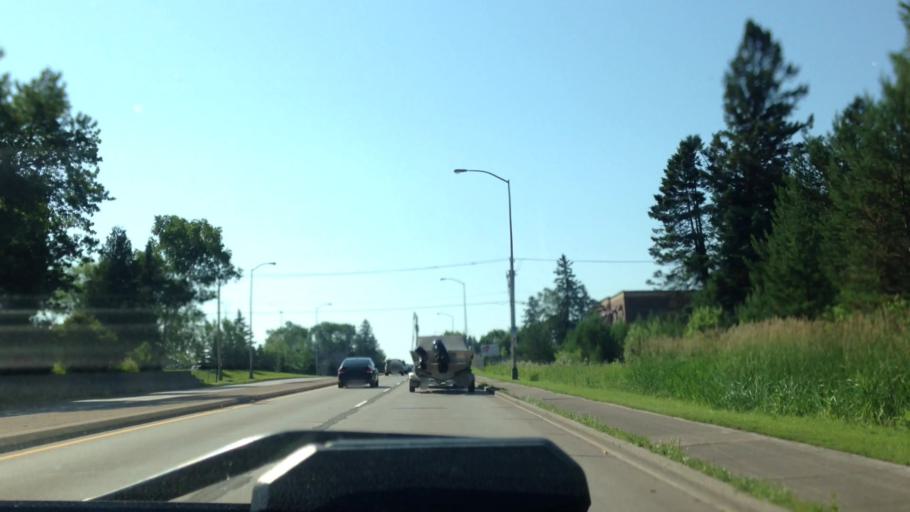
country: US
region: Wisconsin
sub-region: Douglas County
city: Superior
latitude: 46.6927
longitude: -92.0297
